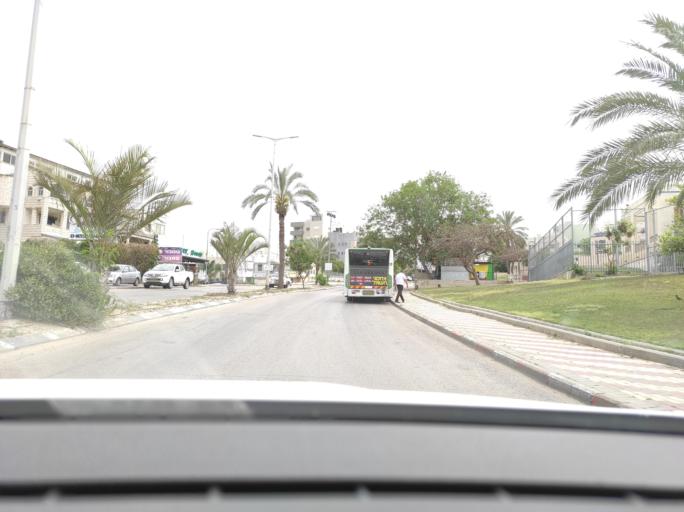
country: IL
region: Central District
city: Kafr Qasim
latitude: 32.1183
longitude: 34.9661
